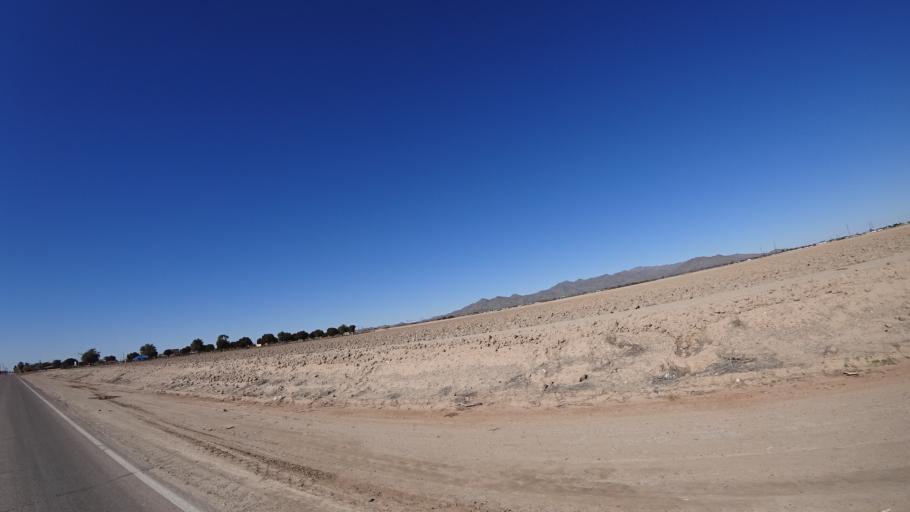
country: US
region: Arizona
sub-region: Maricopa County
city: Buckeye
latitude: 33.4067
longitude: -112.5433
